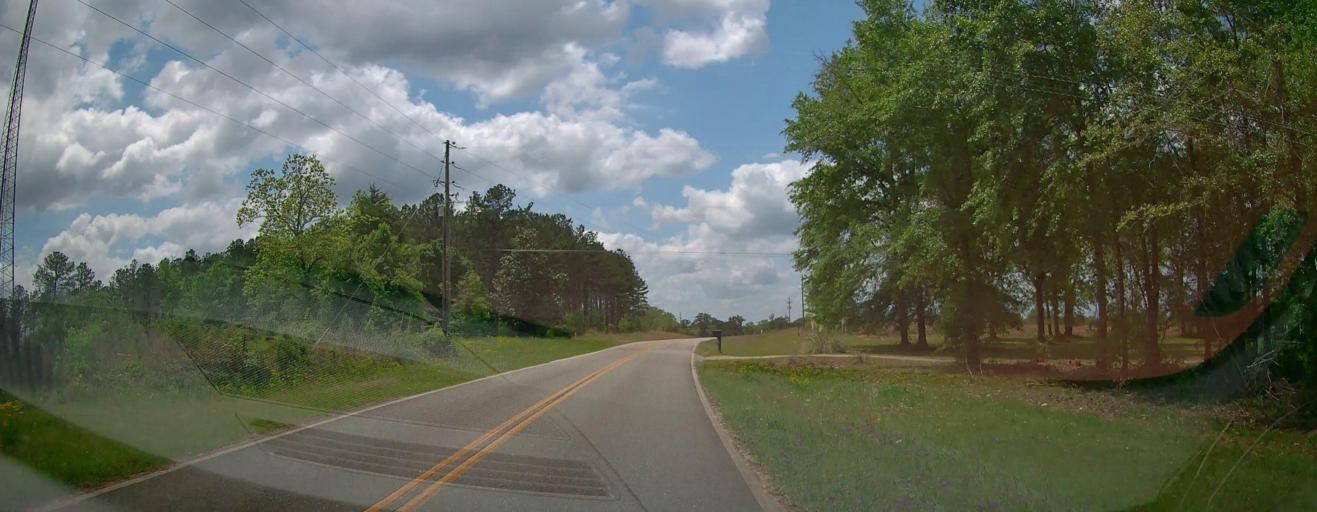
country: US
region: Georgia
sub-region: Laurens County
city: Dublin
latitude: 32.6221
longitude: -82.9907
